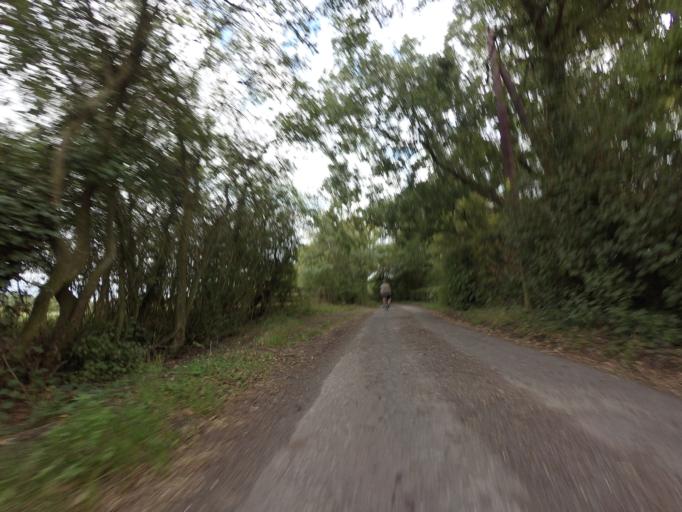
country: GB
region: England
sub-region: Kent
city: Staplehurst
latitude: 51.1936
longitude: 0.5752
